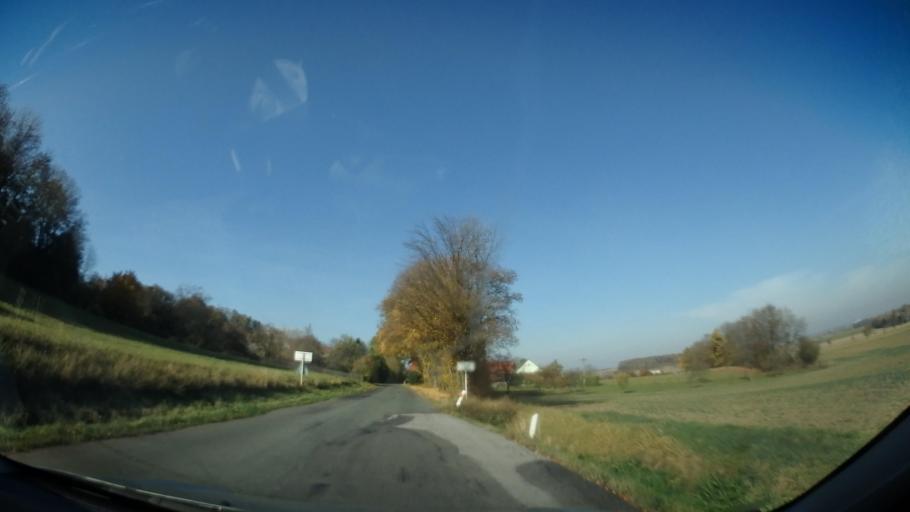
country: CZ
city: Ceske Mezirici
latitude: 50.2403
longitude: 16.0253
